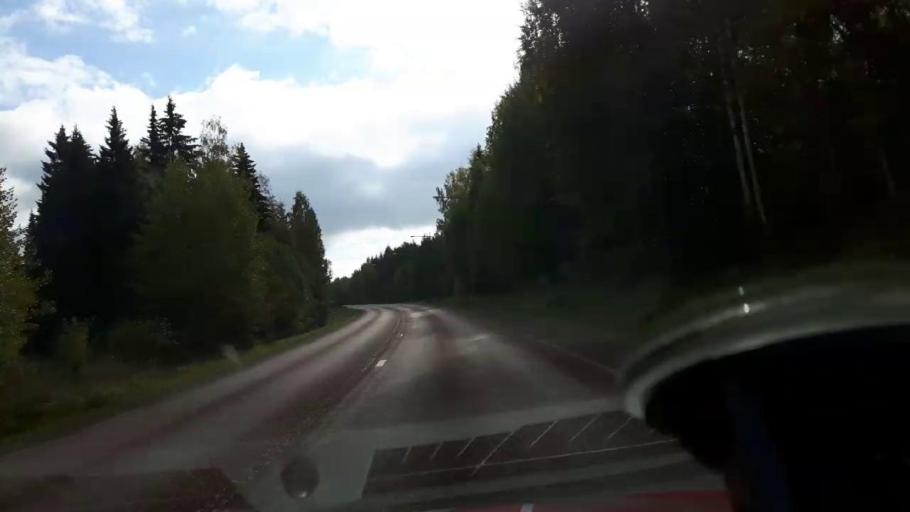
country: SE
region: Gaevleborg
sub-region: Bollnas Kommun
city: Arbra
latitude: 61.5753
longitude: 16.3179
